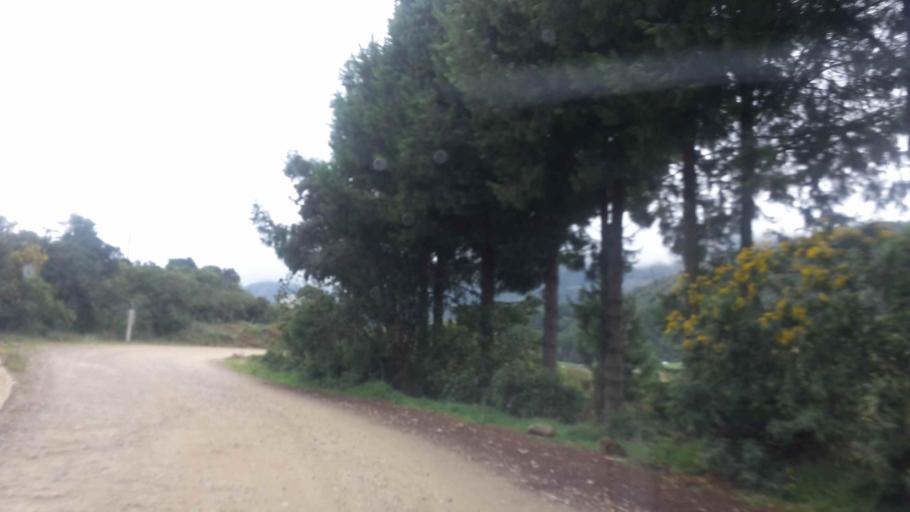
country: BO
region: Cochabamba
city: Totora
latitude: -17.5745
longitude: -65.2863
